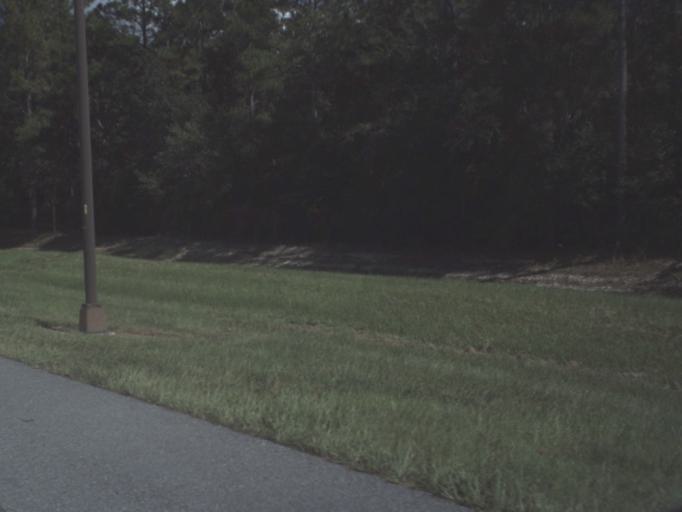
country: US
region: Florida
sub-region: Pasco County
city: Shady Hills
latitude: 28.3969
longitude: -82.5246
